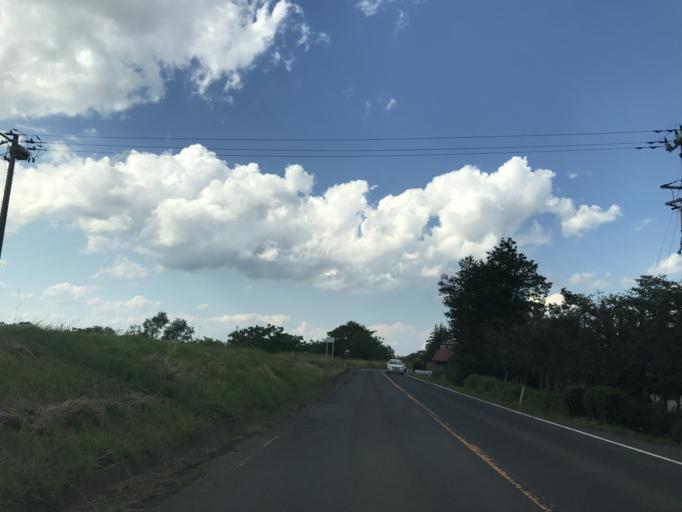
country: JP
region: Miyagi
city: Wakuya
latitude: 38.6755
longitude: 141.2075
